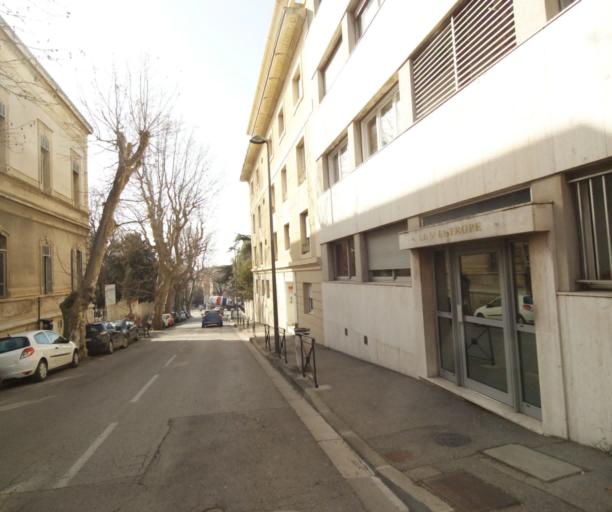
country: FR
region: Provence-Alpes-Cote d'Azur
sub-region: Departement des Bouches-du-Rhone
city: Aix-en-Provence
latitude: 43.5332
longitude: 5.4510
